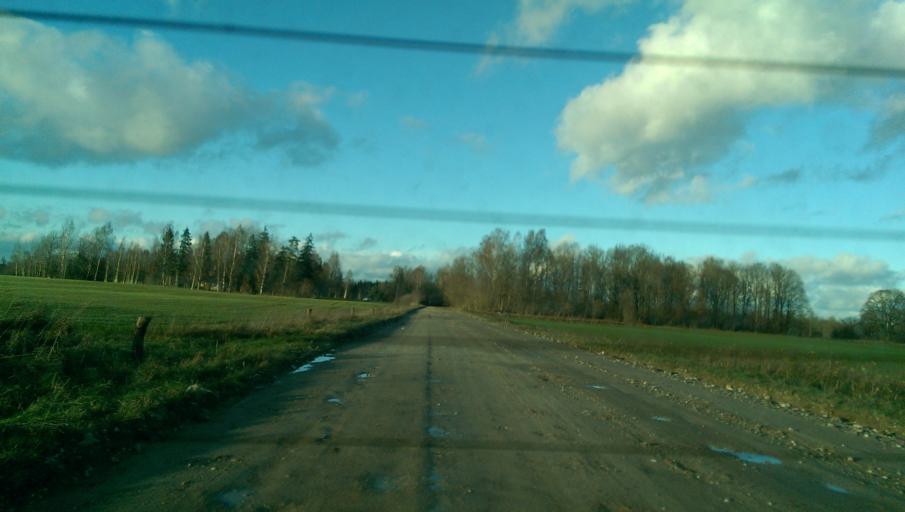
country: LV
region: Aizpute
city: Aizpute
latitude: 56.7471
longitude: 21.7363
